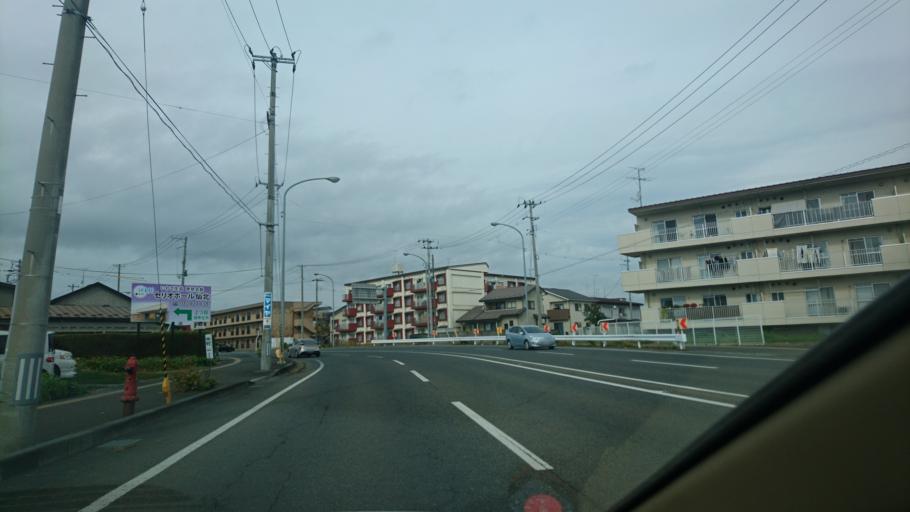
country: JP
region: Iwate
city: Morioka-shi
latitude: 39.6842
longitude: 141.1552
